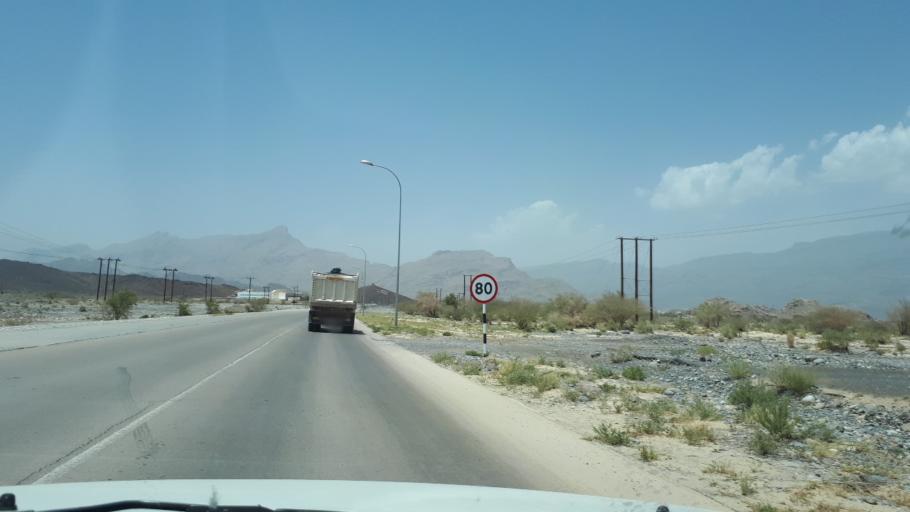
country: OM
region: Muhafazat ad Dakhiliyah
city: Bahla'
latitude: 23.0610
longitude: 57.2813
